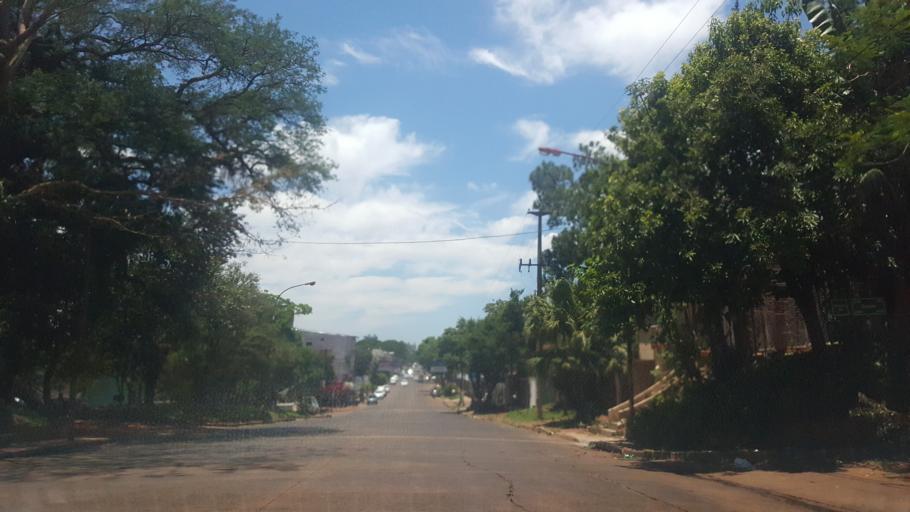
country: AR
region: Misiones
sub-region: Departamento de Capital
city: Posadas
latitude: -27.3686
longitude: -55.9196
